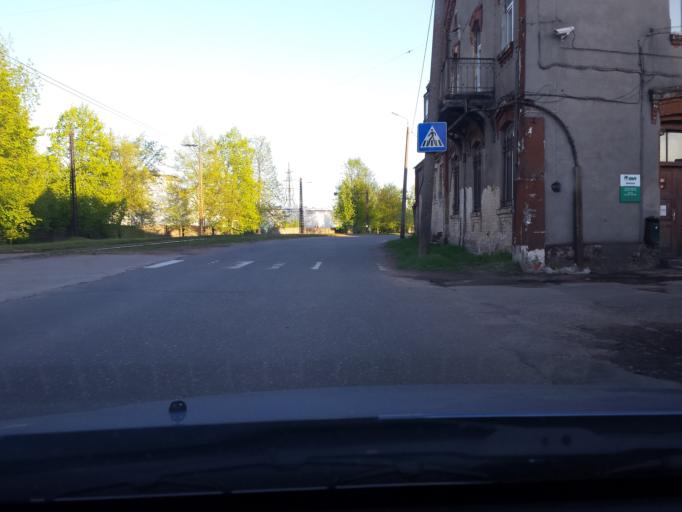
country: LV
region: Riga
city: Jaunciems
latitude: 57.0156
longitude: 24.1236
